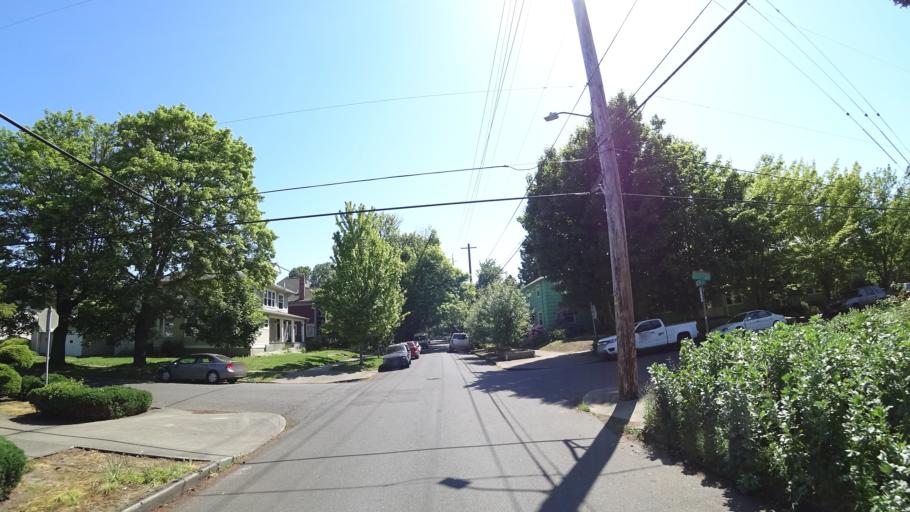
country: US
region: Oregon
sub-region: Multnomah County
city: Portland
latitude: 45.5321
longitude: -122.6432
